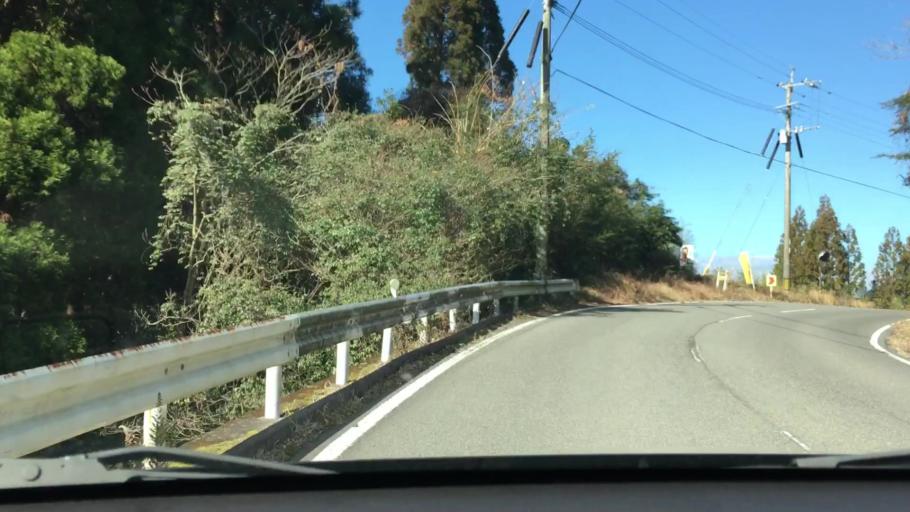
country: JP
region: Kagoshima
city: Ijuin
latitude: 31.7272
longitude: 130.4183
